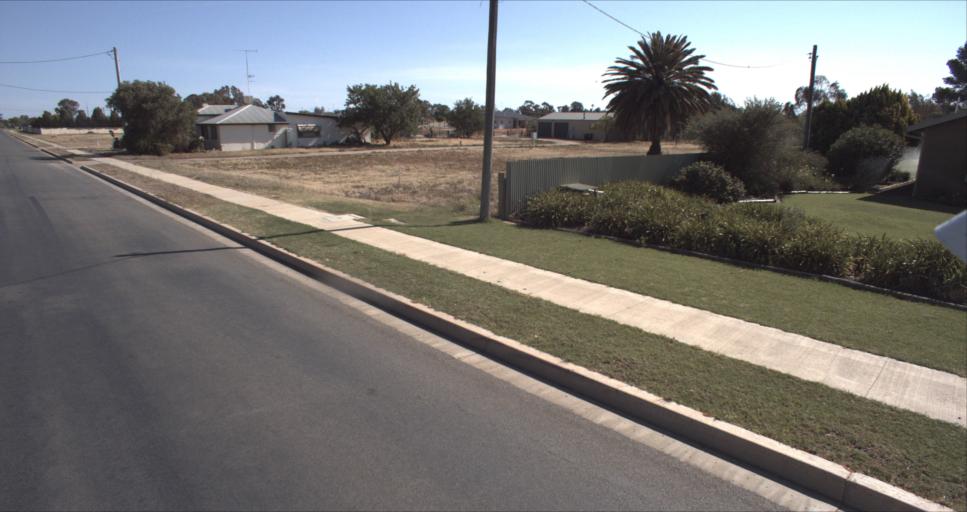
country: AU
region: New South Wales
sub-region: Leeton
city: Leeton
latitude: -34.5477
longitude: 146.4178
